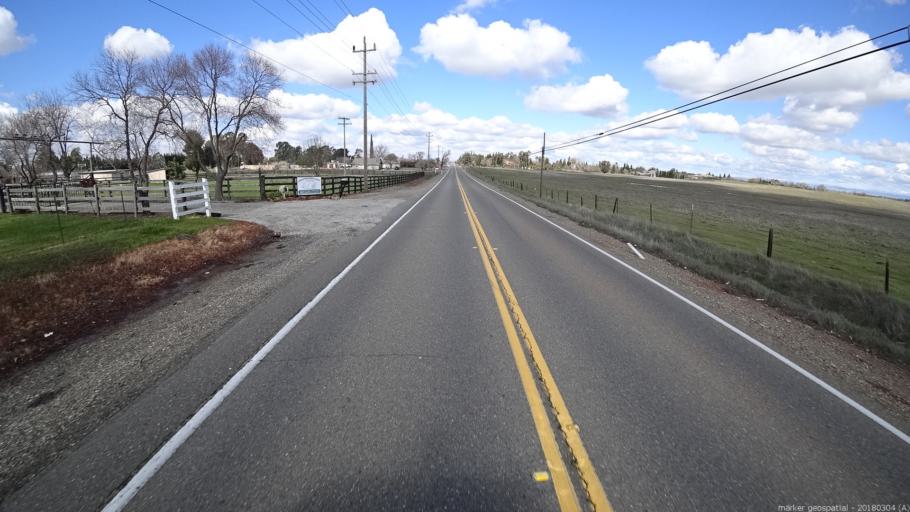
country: US
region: California
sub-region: Sacramento County
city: Vineyard
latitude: 38.4780
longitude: -121.2977
